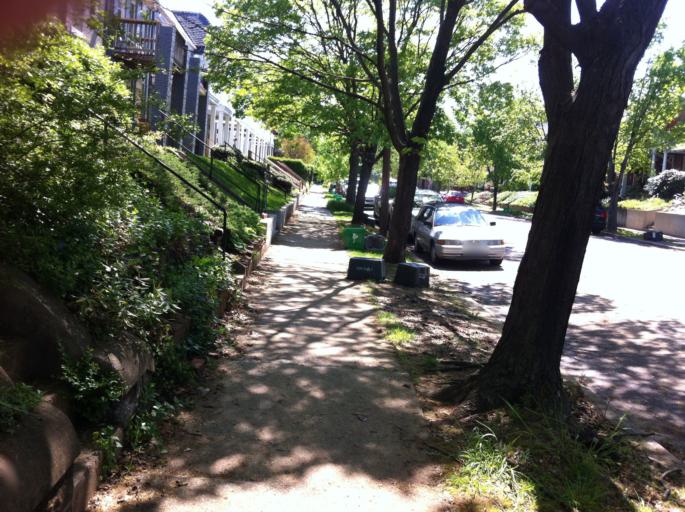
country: US
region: Virginia
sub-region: City of Richmond
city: Richmond
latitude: 37.5584
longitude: -77.4800
